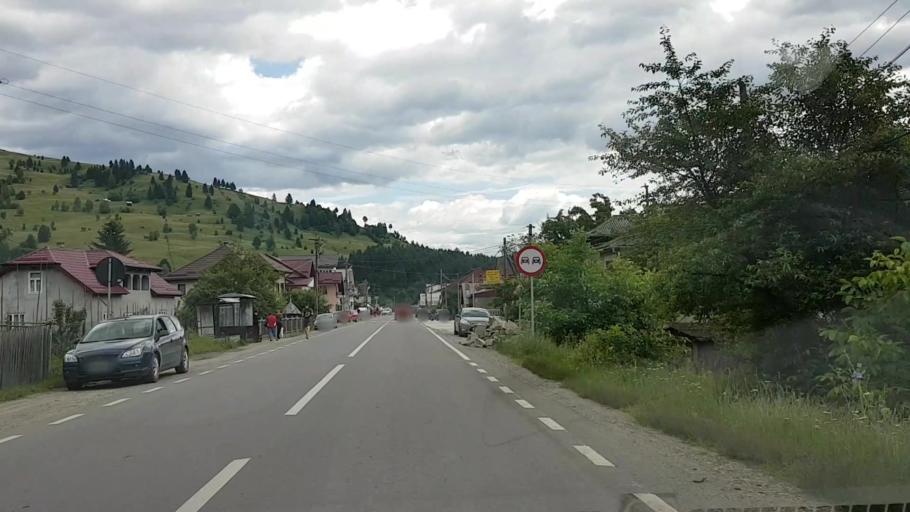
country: RO
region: Neamt
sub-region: Comuna Borca
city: Borca
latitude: 47.1807
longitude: 25.7830
